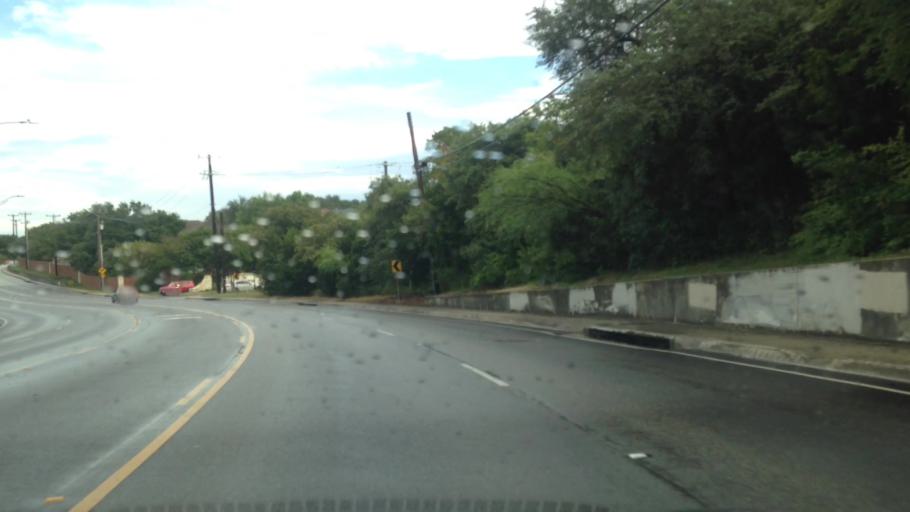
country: US
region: Texas
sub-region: Bexar County
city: Live Oak
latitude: 29.5937
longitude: -98.4012
